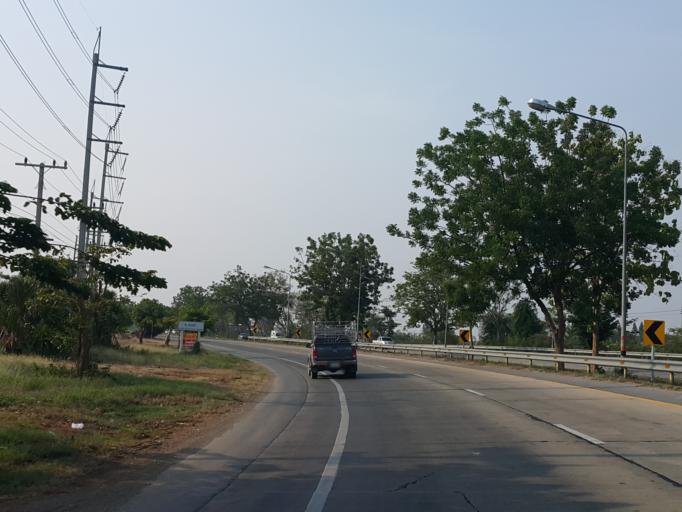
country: TH
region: Suphan Buri
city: Doem Bang Nang Buat
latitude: 14.9244
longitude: 100.0857
